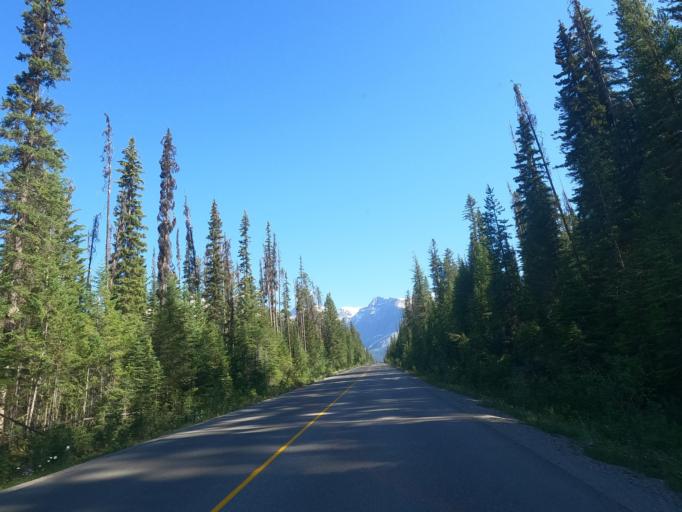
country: CA
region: Alberta
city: Lake Louise
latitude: 51.3946
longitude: -116.5356
